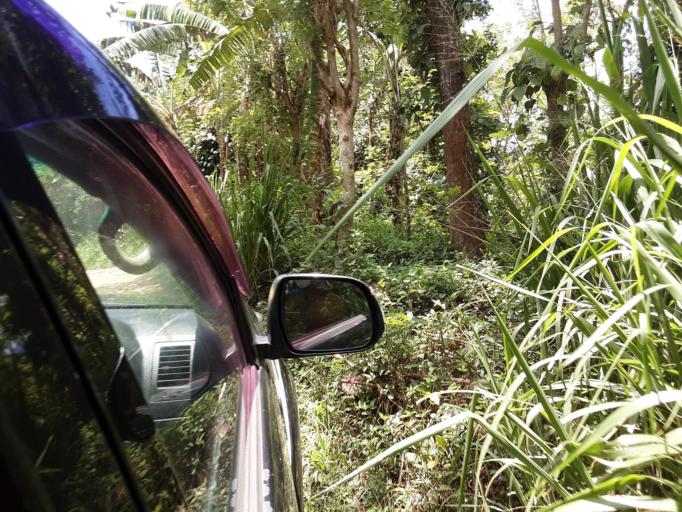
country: LK
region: Uva
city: Haputale
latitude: 6.8230
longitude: 81.1099
